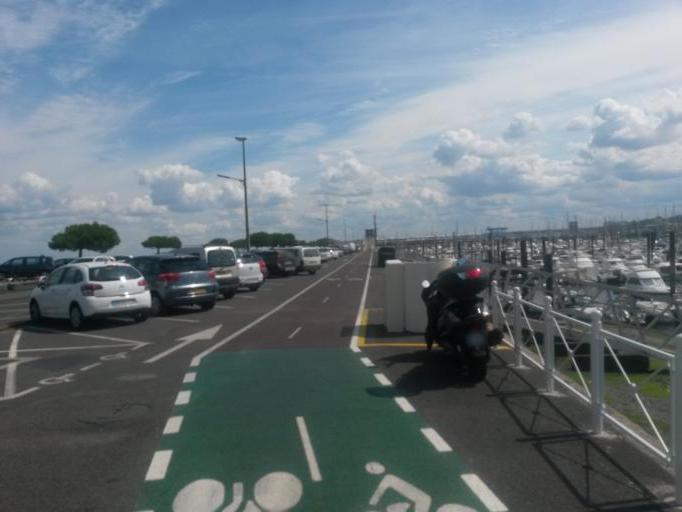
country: FR
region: Aquitaine
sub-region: Departement de la Gironde
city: Arcachon
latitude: 44.6618
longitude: -1.1493
